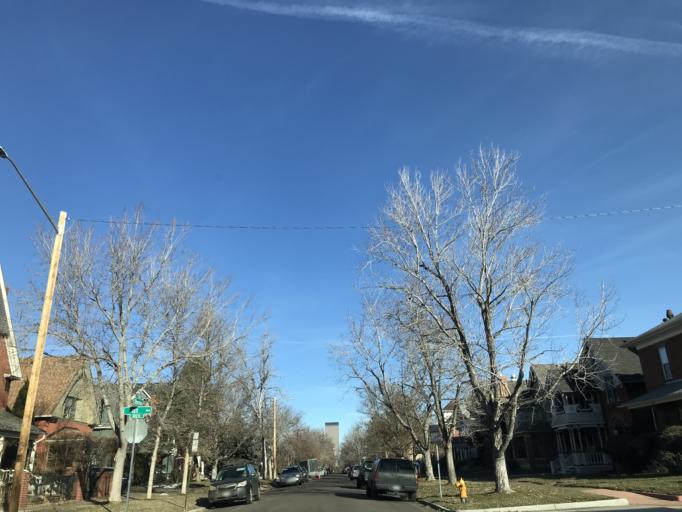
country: US
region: Colorado
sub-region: Denver County
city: Denver
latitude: 39.7182
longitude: -104.9850
